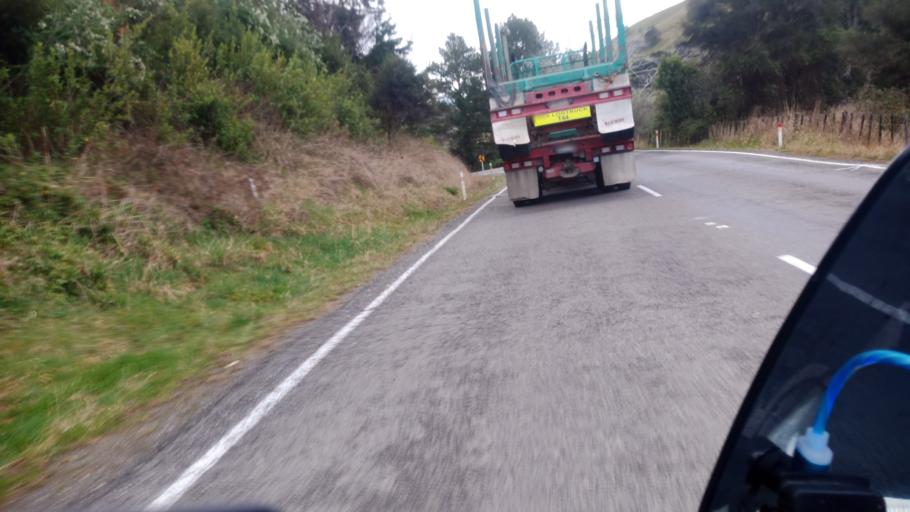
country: NZ
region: Gisborne
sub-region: Gisborne District
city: Gisborne
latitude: -38.0519
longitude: 178.3031
